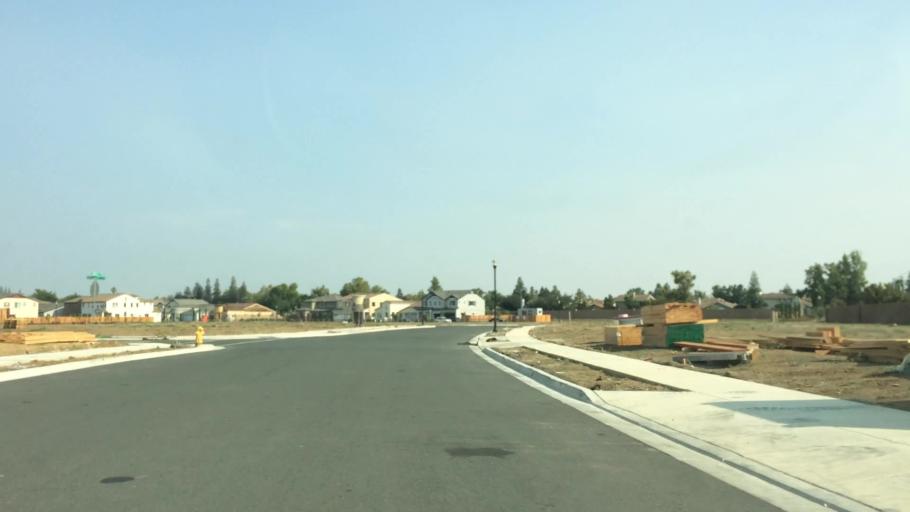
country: US
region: California
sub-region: Contra Costa County
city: Brentwood
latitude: 37.9276
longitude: -121.7053
